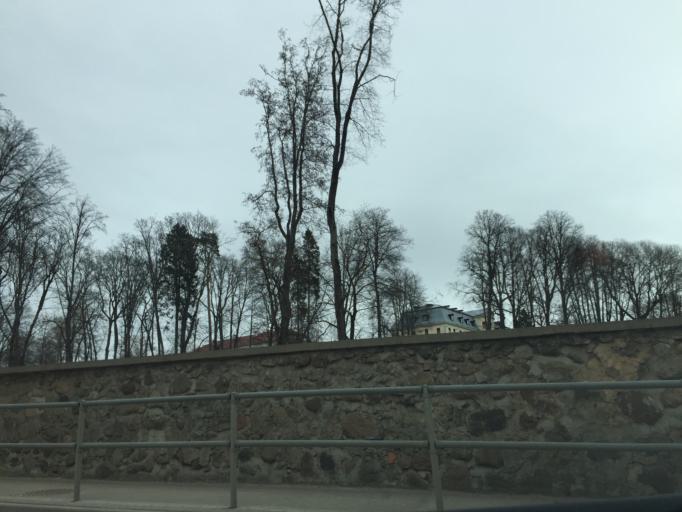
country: LV
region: Kraslavas Rajons
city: Kraslava
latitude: 55.8995
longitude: 27.1563
